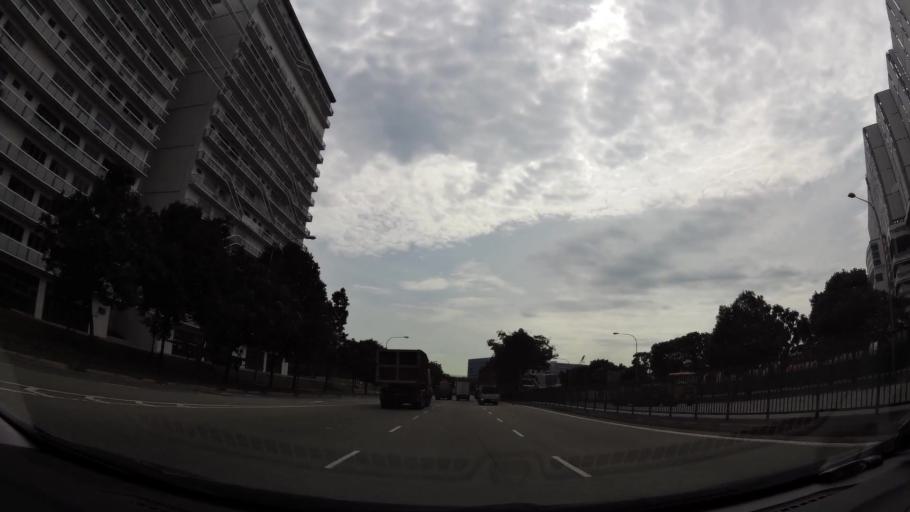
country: SG
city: Singapore
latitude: 1.3151
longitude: 103.6968
